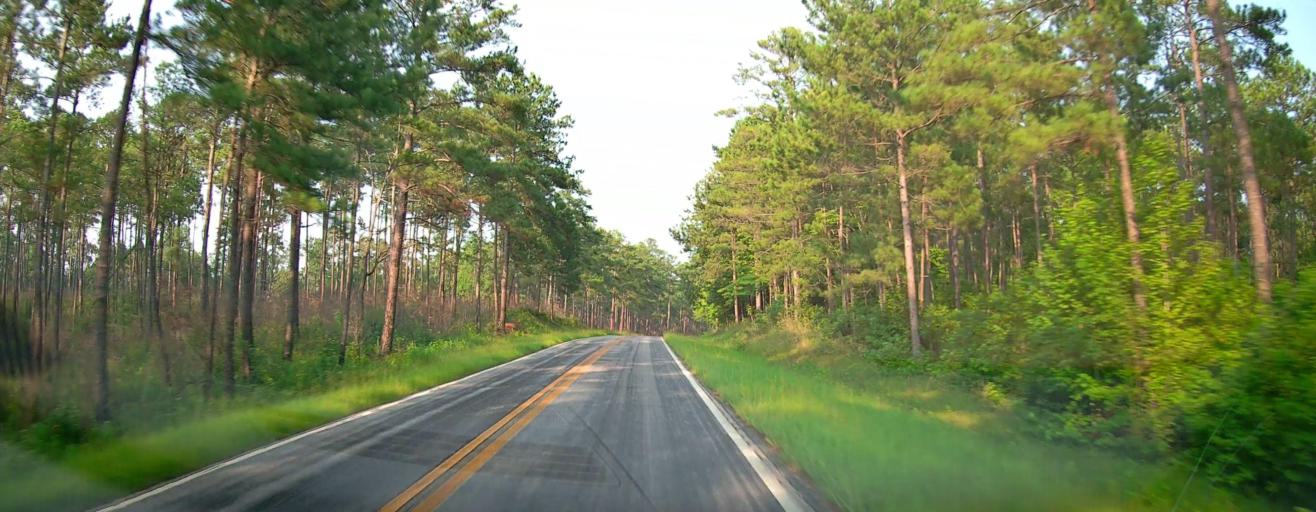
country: US
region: Georgia
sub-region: Jones County
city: Gray
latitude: 33.0955
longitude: -83.7036
